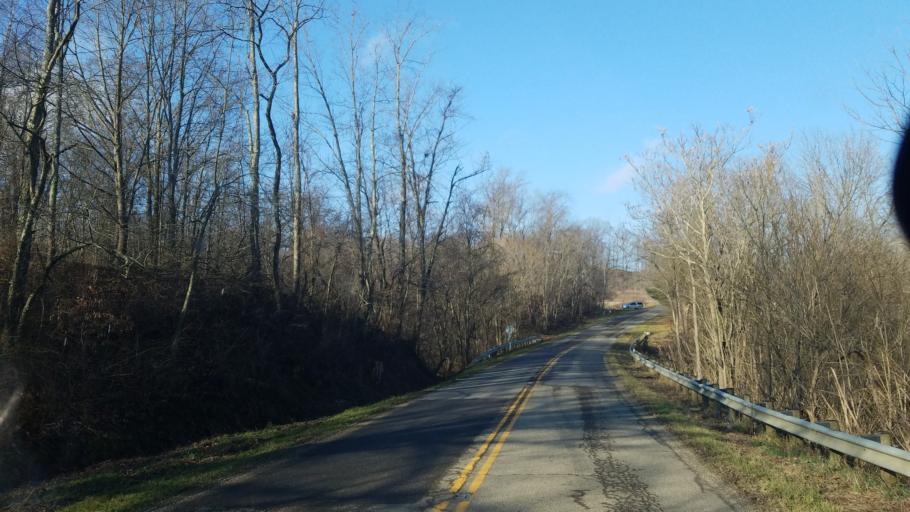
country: US
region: Ohio
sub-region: Guernsey County
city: Byesville
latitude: 40.0365
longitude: -81.4108
